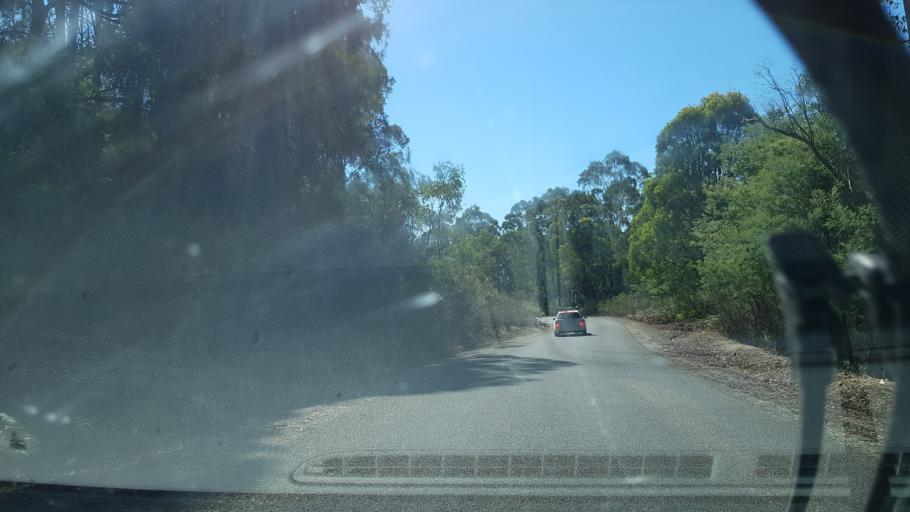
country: AU
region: Victoria
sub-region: Mansfield
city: Mansfield
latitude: -36.9010
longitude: 146.3903
